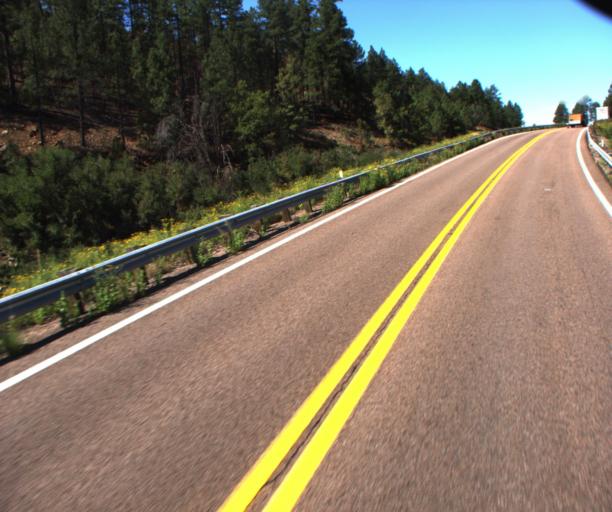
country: US
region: Arizona
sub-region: Navajo County
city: Linden
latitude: 34.0688
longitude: -110.1955
